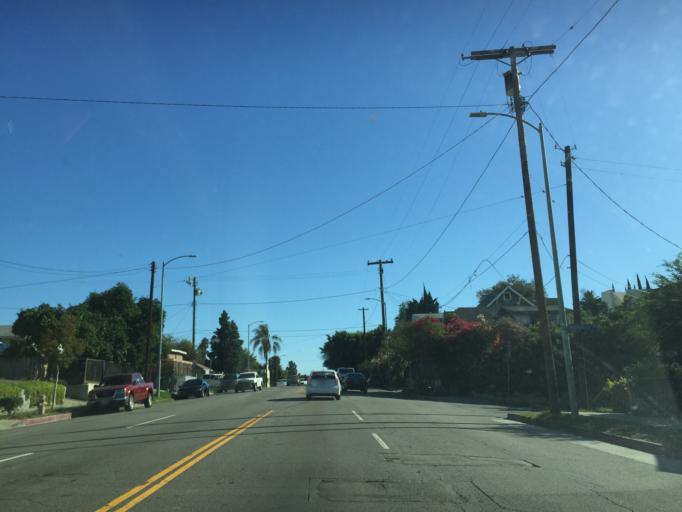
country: US
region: California
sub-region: Los Angeles County
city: Silver Lake
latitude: 34.0802
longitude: -118.2868
